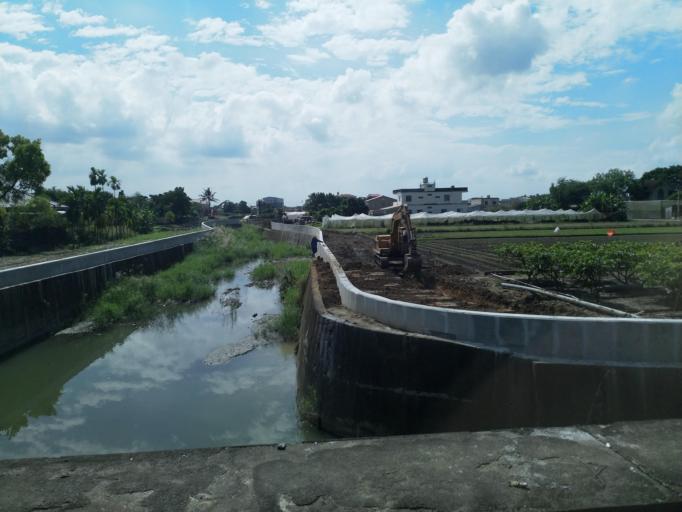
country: TW
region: Taiwan
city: Yujing
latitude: 22.9051
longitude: 120.5273
